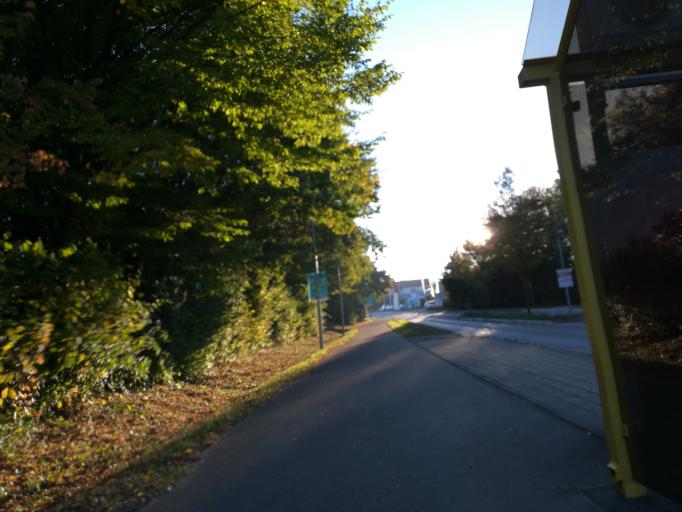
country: DE
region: Baden-Wuerttemberg
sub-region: Regierungsbezirk Stuttgart
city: Filderstadt
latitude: 48.6600
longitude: 9.1995
